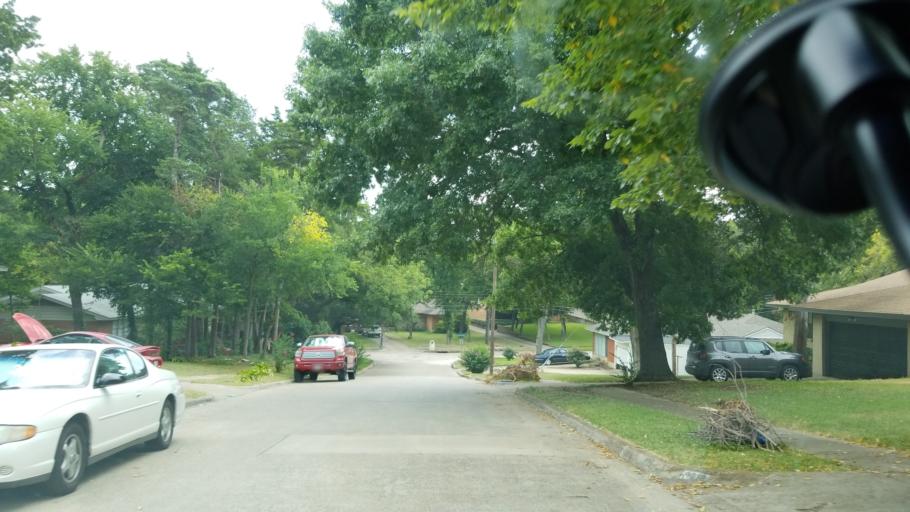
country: US
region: Texas
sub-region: Dallas County
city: Cockrell Hill
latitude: 32.6879
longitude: -96.8505
